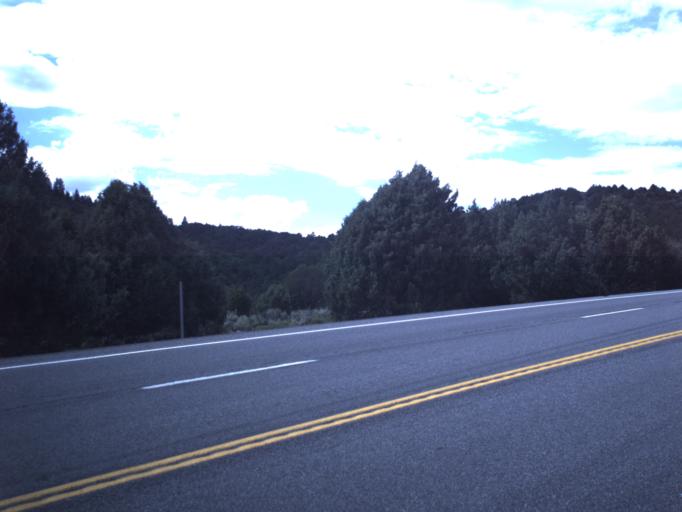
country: US
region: Utah
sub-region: Garfield County
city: Panguitch
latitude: 38.0236
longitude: -112.5319
